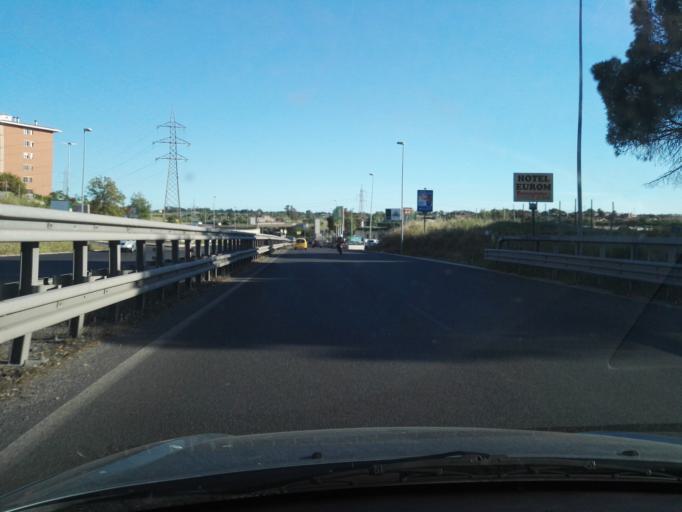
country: IT
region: Latium
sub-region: Citta metropolitana di Roma Capitale
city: Selcetta
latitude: 41.7939
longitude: 12.4807
